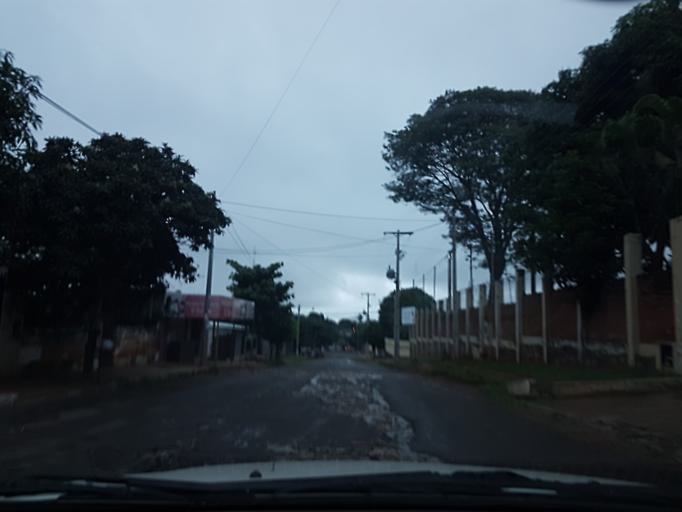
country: PY
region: Central
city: Villa Elisa
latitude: -25.3539
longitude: -57.5678
